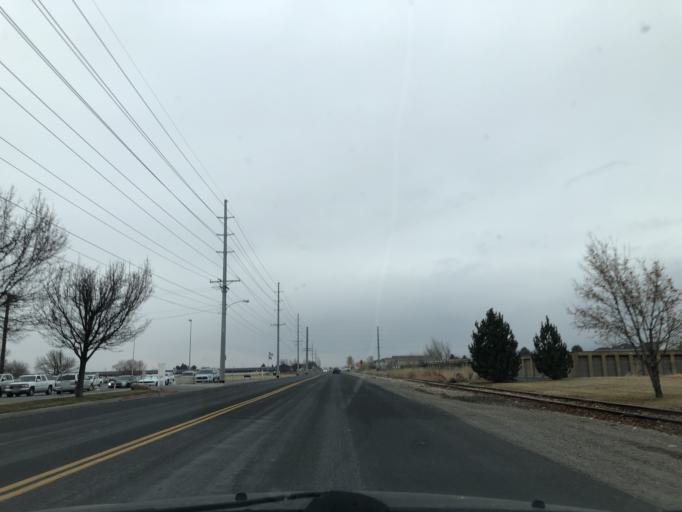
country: US
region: Utah
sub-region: Cache County
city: Logan
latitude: 41.7479
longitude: -111.8493
